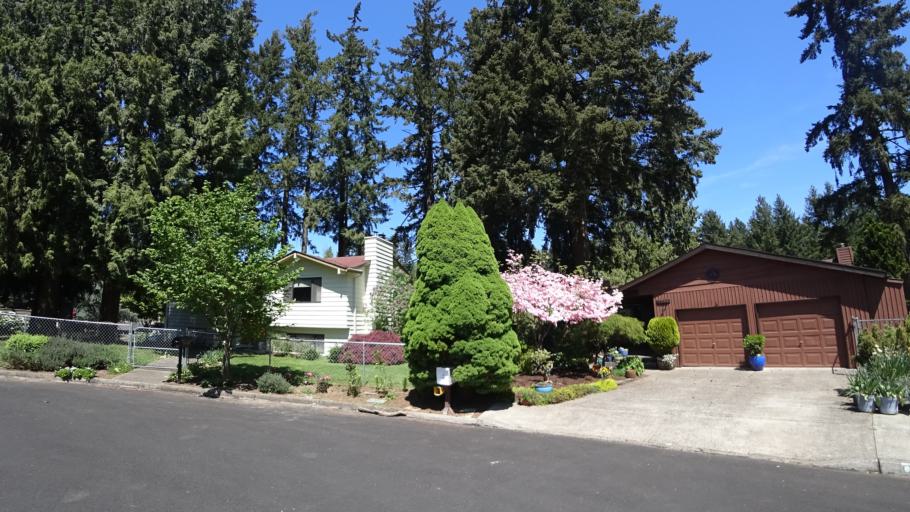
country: US
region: Oregon
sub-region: Washington County
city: Hillsboro
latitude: 45.5159
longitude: -122.9600
